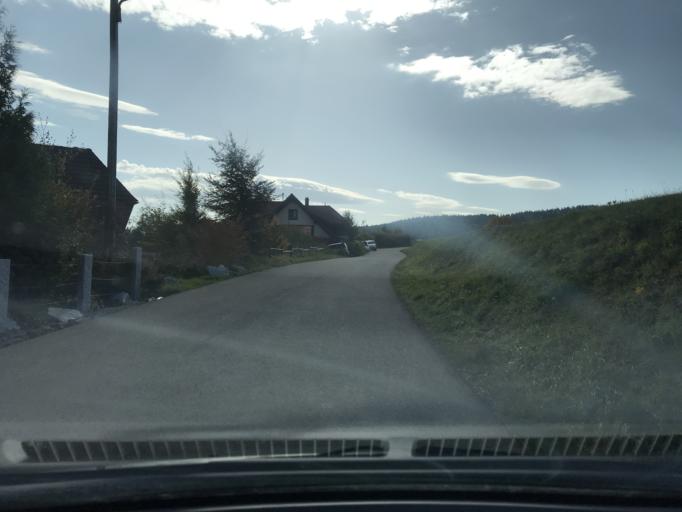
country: DE
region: Baden-Wuerttemberg
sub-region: Freiburg Region
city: Herrischried
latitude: 47.6715
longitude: 7.9886
